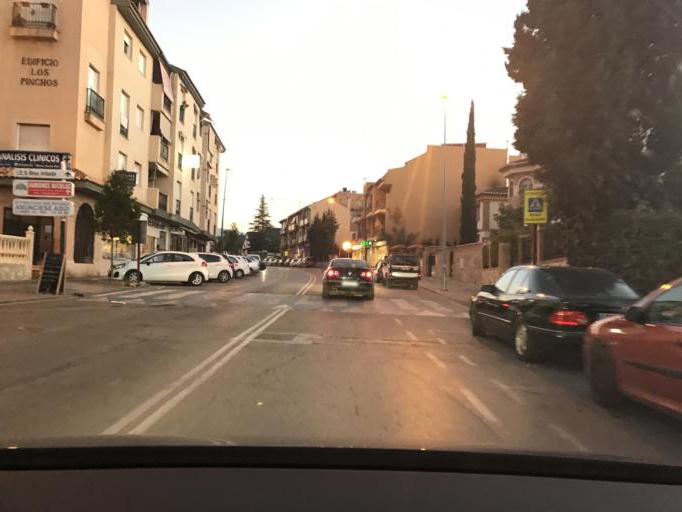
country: ES
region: Andalusia
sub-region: Provincia de Granada
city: Ogijares
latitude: 37.1201
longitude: -3.6049
